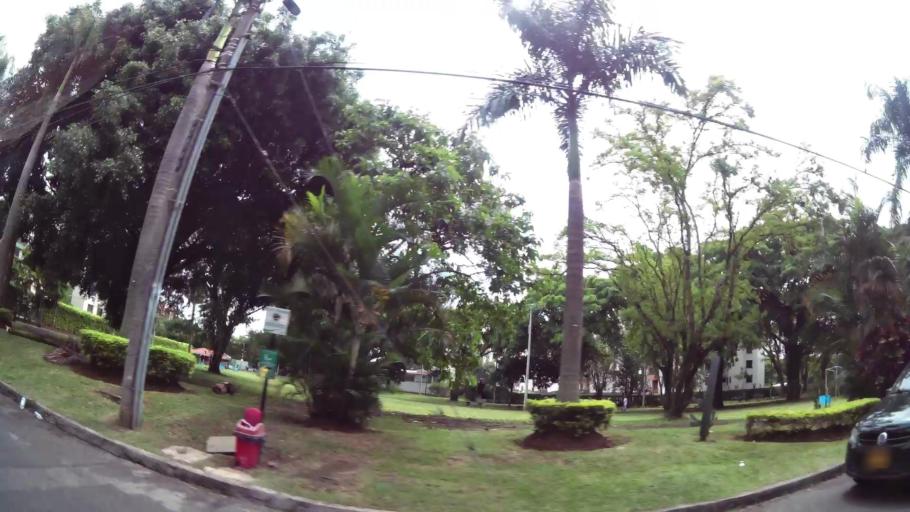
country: CO
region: Valle del Cauca
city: Cali
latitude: 3.3967
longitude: -76.5368
